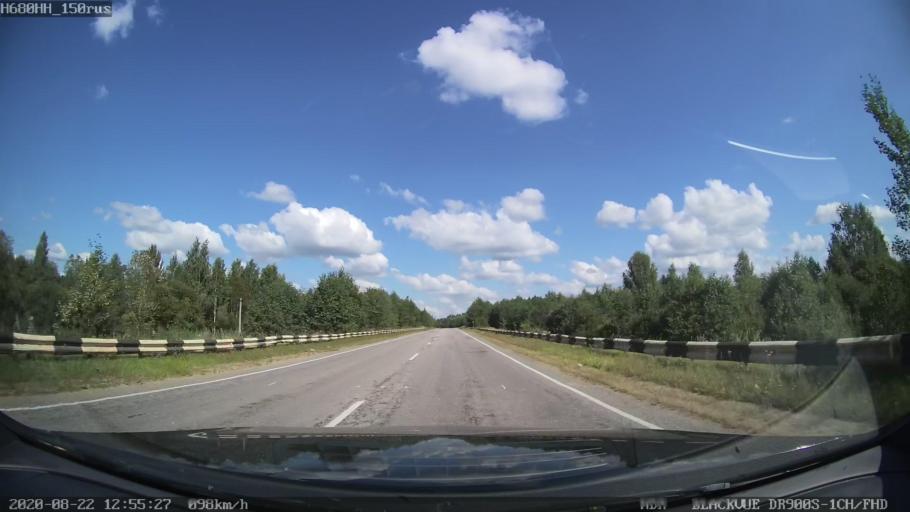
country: RU
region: Tverskaya
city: Rameshki
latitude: 57.5438
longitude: 36.3018
